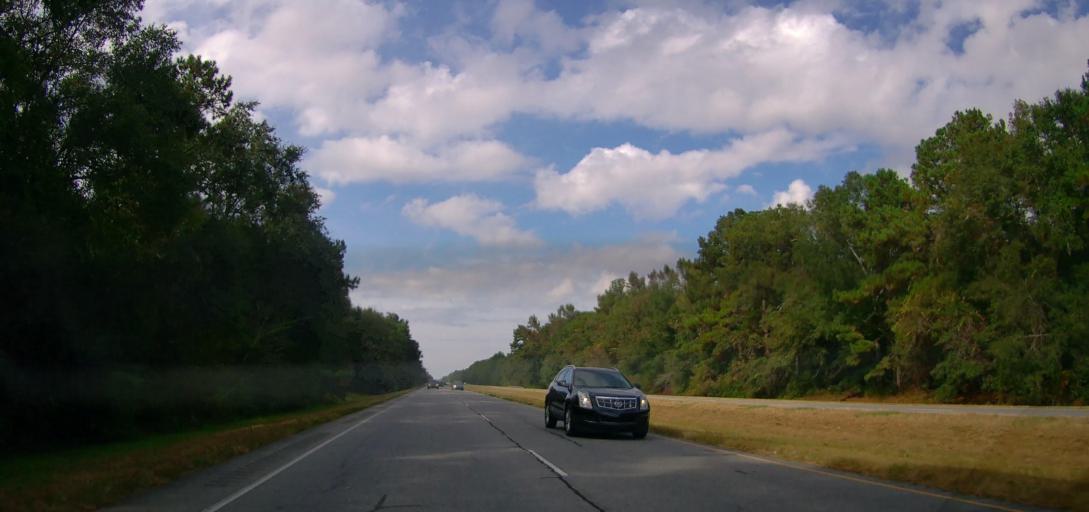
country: US
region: Georgia
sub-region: Mitchell County
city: Pelham
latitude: 31.1806
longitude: -84.1533
